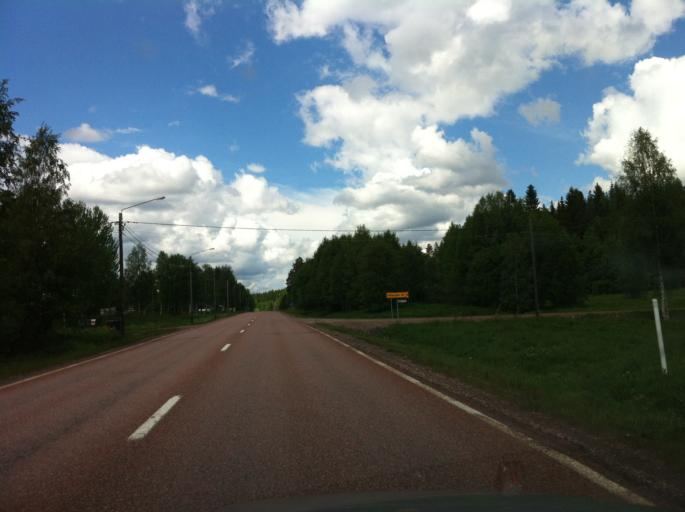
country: SE
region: Dalarna
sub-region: Malung-Saelens kommun
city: Malung
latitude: 60.9063
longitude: 13.3829
